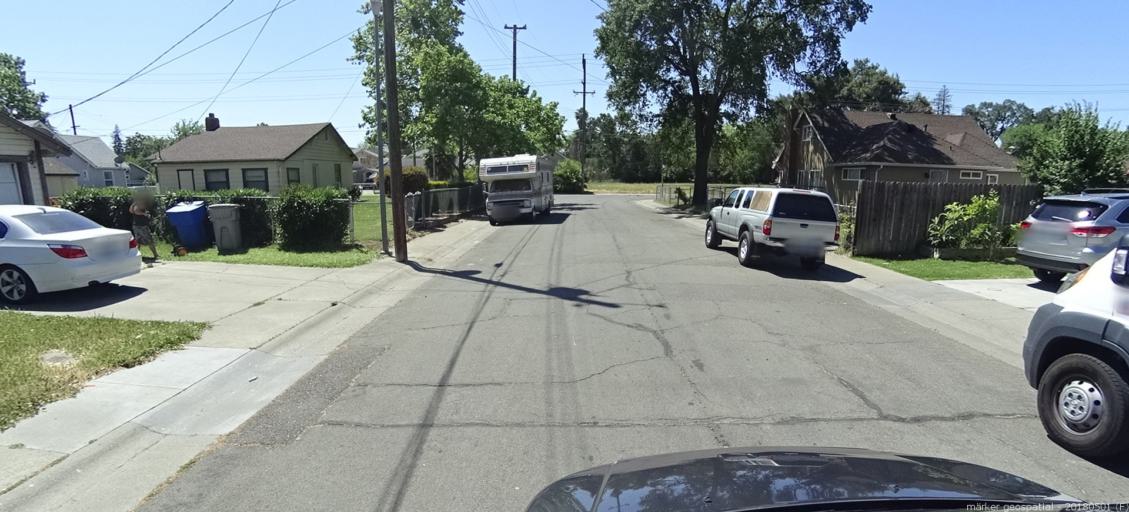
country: US
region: California
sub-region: Sacramento County
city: Rio Linda
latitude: 38.6321
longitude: -121.4367
